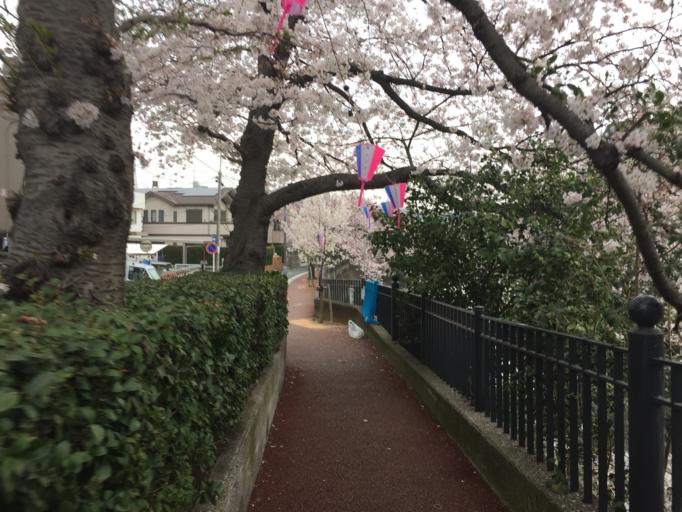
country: JP
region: Kanagawa
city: Yokohama
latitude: 35.4308
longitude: 139.6076
